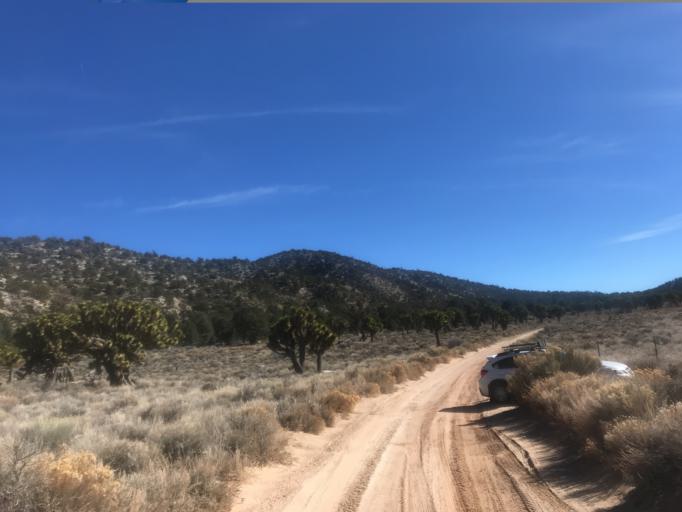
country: US
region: California
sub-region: San Bernardino County
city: Big Bear City
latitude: 34.2523
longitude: -116.7068
